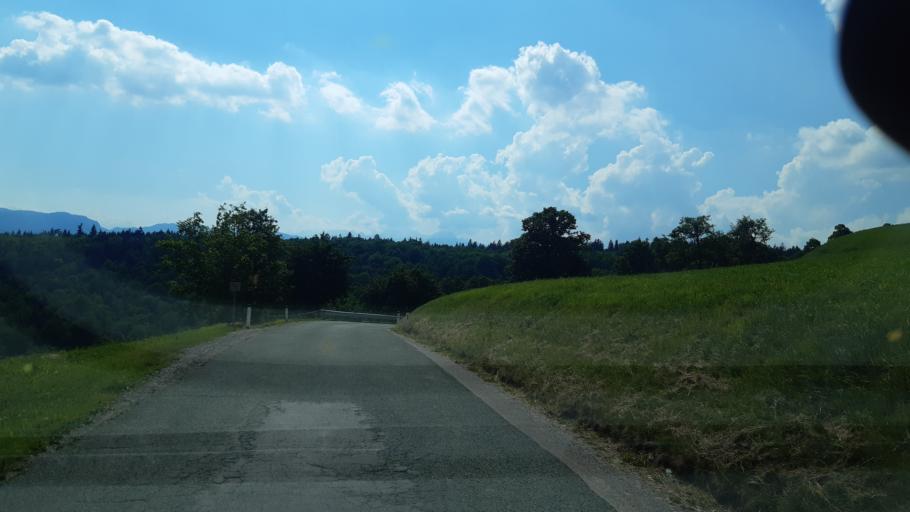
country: SI
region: Radovljica
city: Radovljica
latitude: 46.3690
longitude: 14.2233
